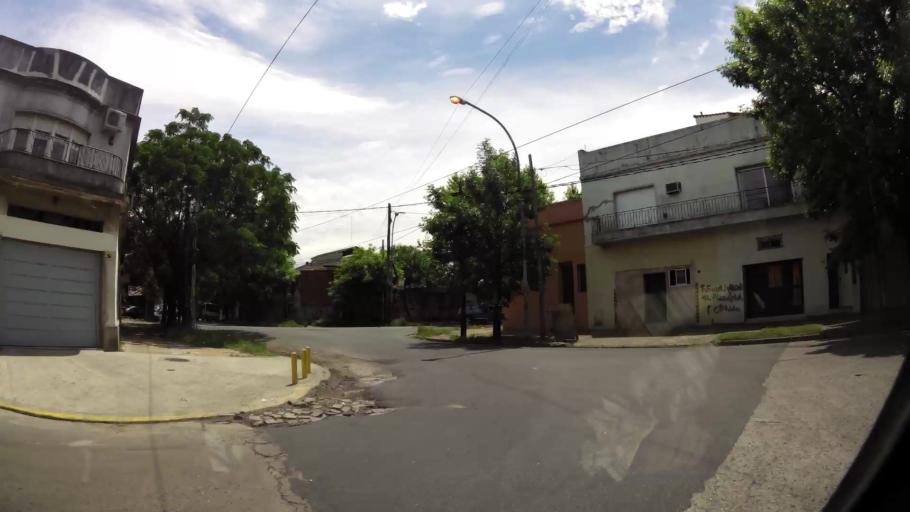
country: AR
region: Buenos Aires
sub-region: Partido de Lanus
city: Lanus
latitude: -34.6653
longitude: -58.4158
